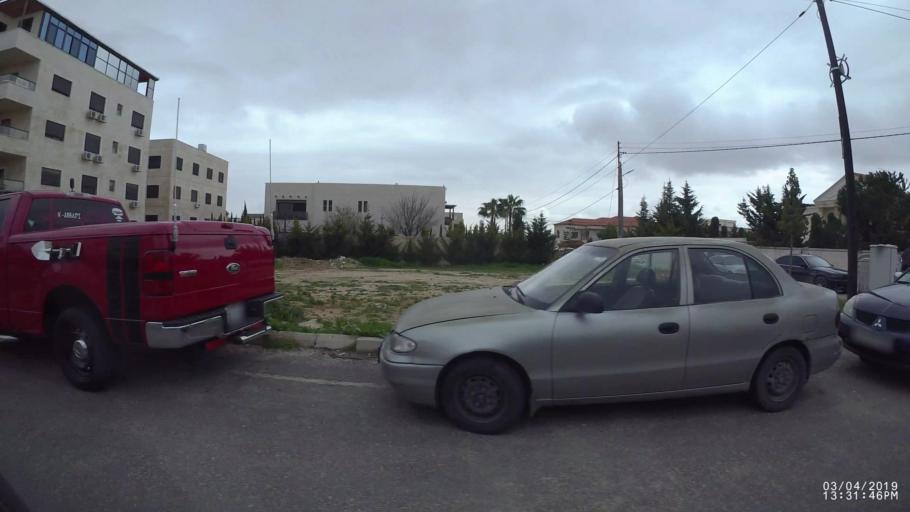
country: JO
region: Amman
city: Wadi as Sir
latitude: 31.9676
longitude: 35.8270
